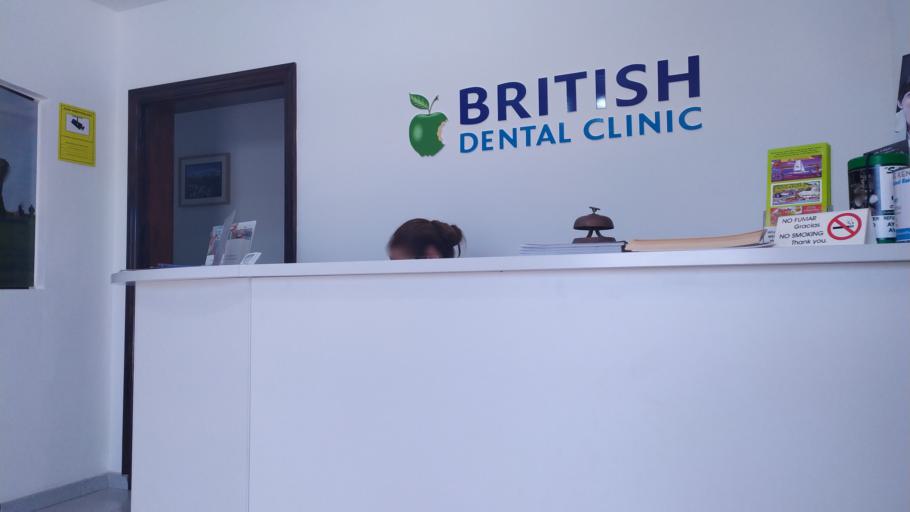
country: ES
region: Canary Islands
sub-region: Provincia de Las Palmas
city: Tias
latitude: 28.9463
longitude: -13.6526
